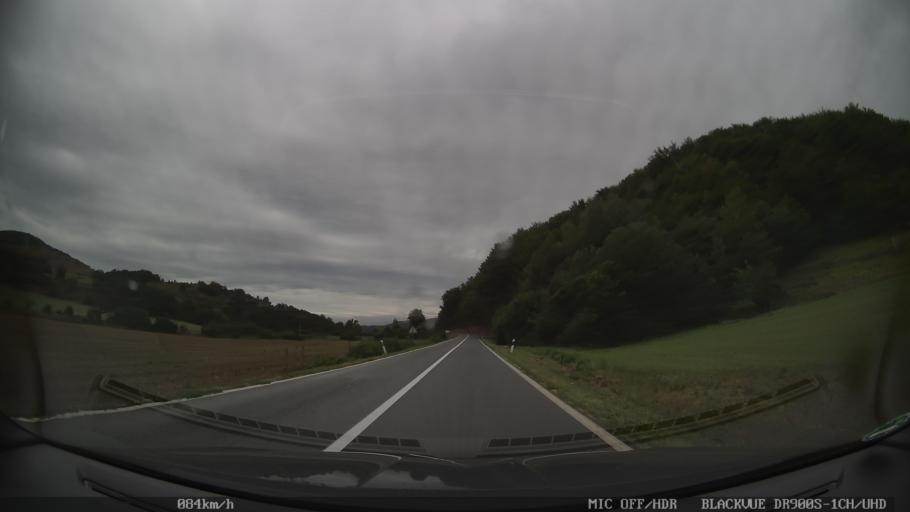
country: HR
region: Licko-Senjska
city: Brinje
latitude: 44.9311
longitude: 15.1334
